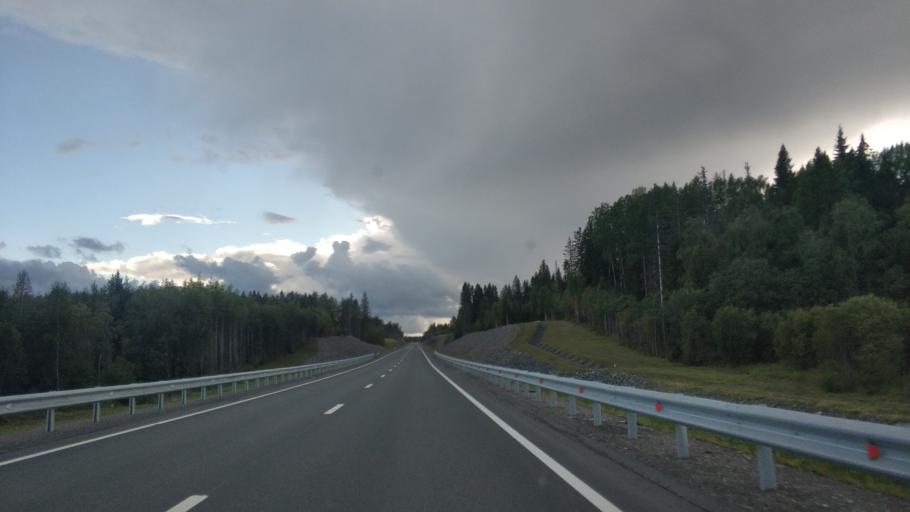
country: RU
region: Republic of Karelia
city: Lakhdenpokh'ya
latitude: 61.4426
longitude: 29.9867
